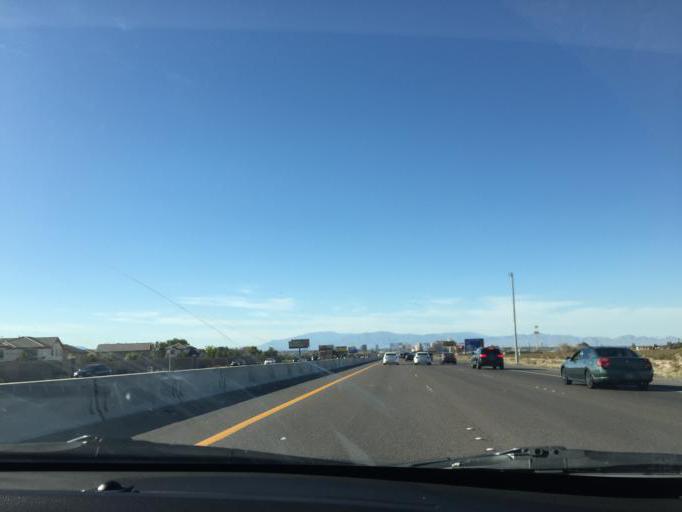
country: US
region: Nevada
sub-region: Clark County
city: Enterprise
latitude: 35.9750
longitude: -115.1812
